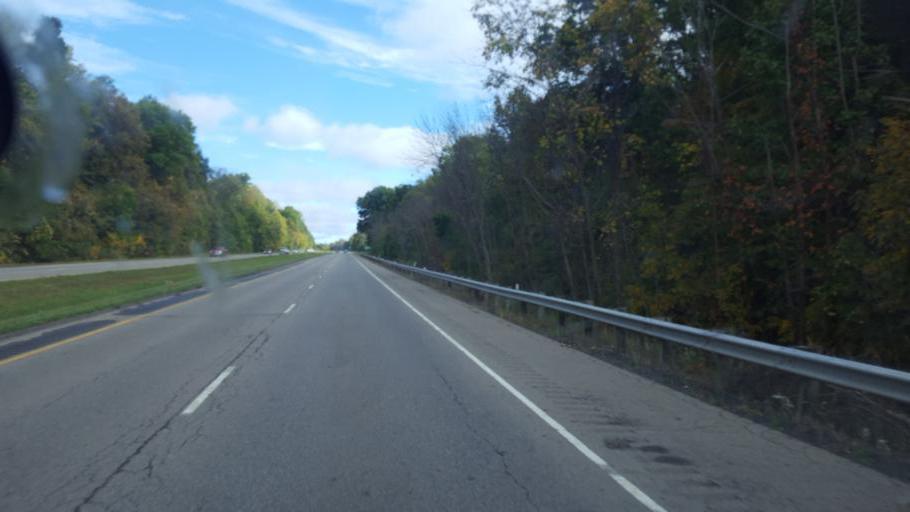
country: US
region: Ohio
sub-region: Richland County
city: Mansfield
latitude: 40.7138
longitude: -82.5033
